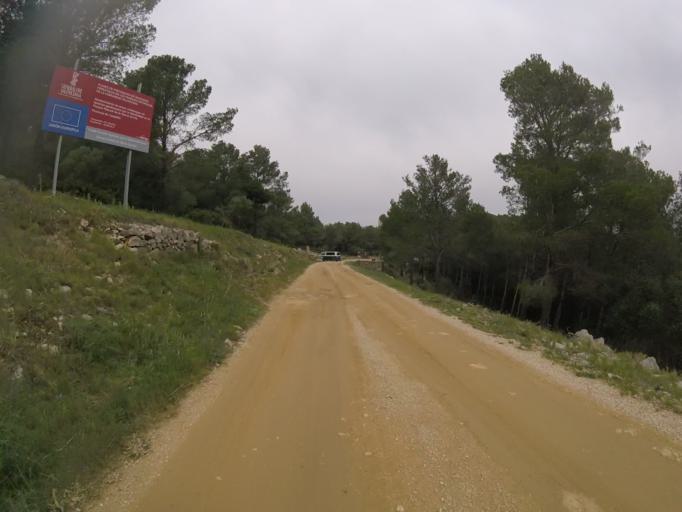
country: ES
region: Valencia
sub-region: Provincia de Castello
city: Alcala de Xivert
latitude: 40.3058
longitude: 0.2559
